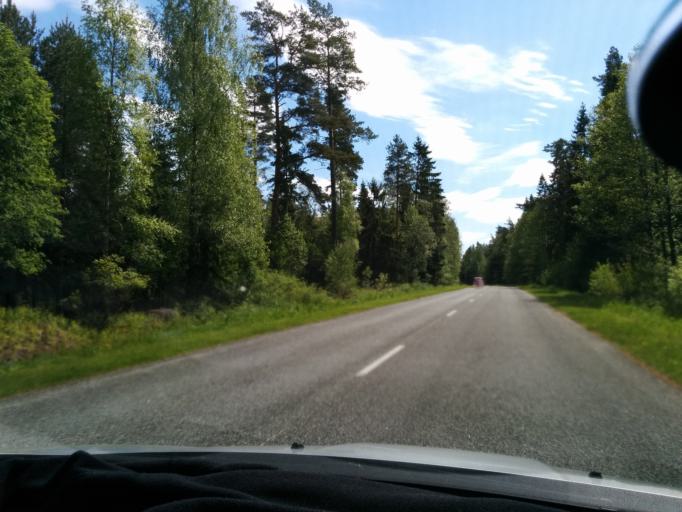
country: EE
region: Harju
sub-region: Loksa linn
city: Loksa
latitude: 59.5733
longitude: 25.9309
